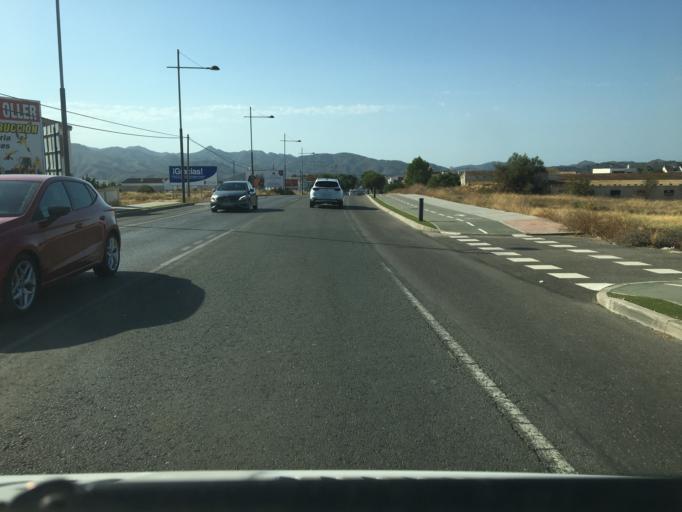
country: ES
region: Andalusia
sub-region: Provincia de Almeria
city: Huercal-Overa
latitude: 37.4056
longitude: -1.9565
